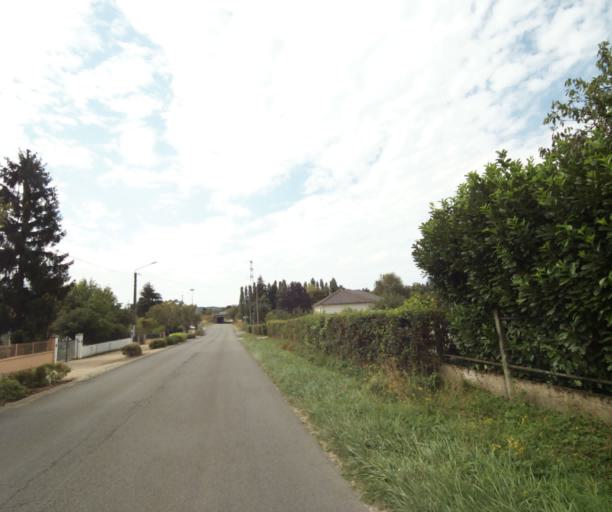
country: FR
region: Bourgogne
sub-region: Departement de Saone-et-Loire
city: Tournus
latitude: 46.5573
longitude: 4.9030
